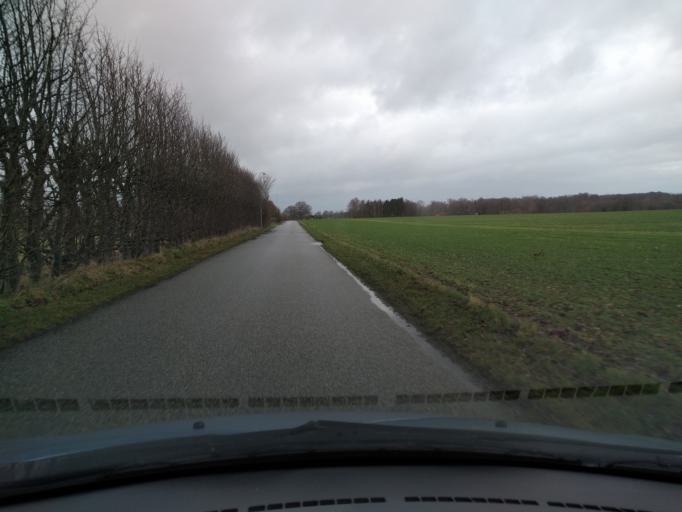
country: DK
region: South Denmark
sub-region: Kerteminde Kommune
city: Langeskov
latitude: 55.3449
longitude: 10.5453
